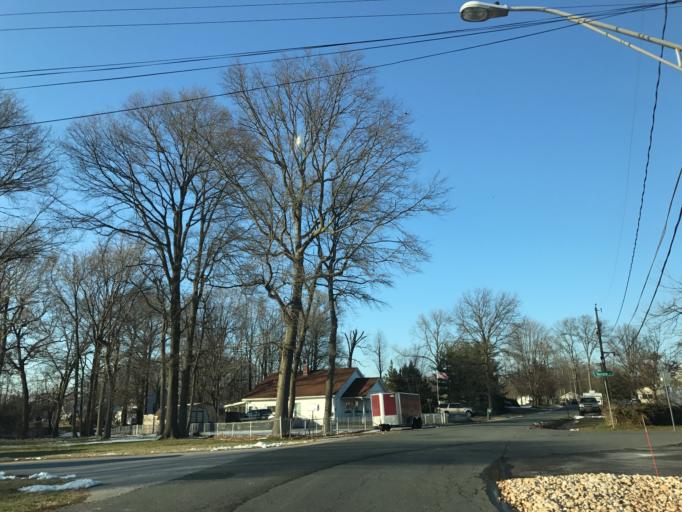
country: US
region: Maryland
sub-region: Baltimore County
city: Essex
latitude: 39.2850
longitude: -76.4432
